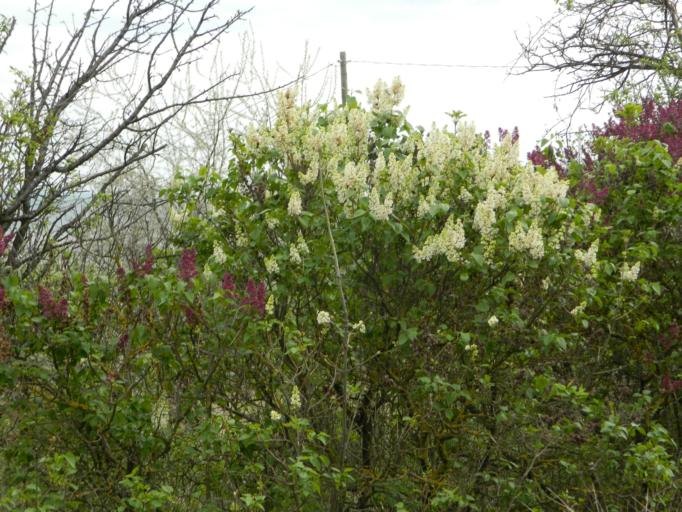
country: HU
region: Veszprem
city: Osi
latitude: 47.2183
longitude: 18.2166
